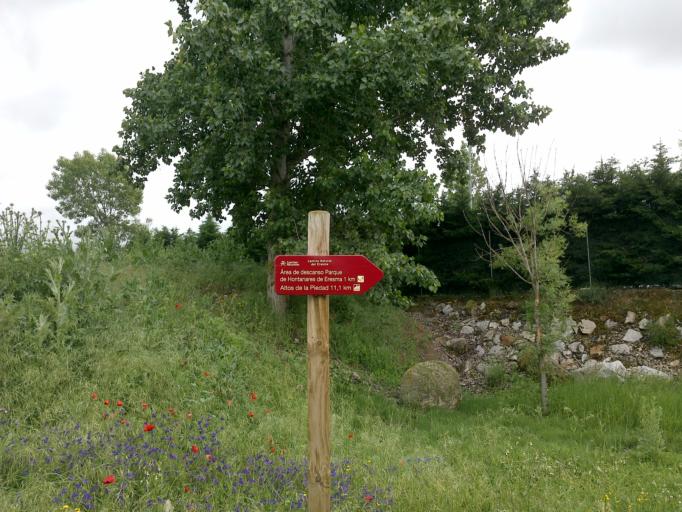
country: ES
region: Castille and Leon
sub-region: Provincia de Segovia
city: Hontanares de Eresma
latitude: 40.9883
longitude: -4.2082
